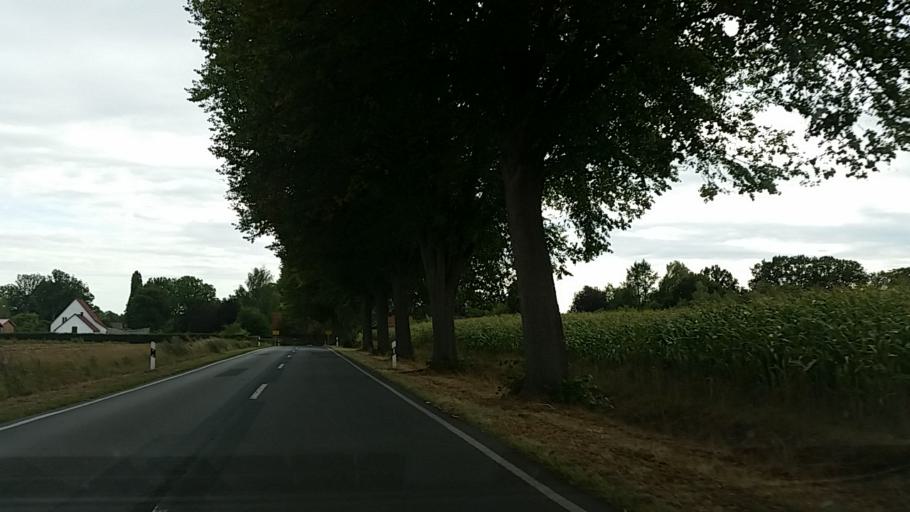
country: DE
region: Lower Saxony
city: Gerdau
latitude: 52.9739
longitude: 10.3952
